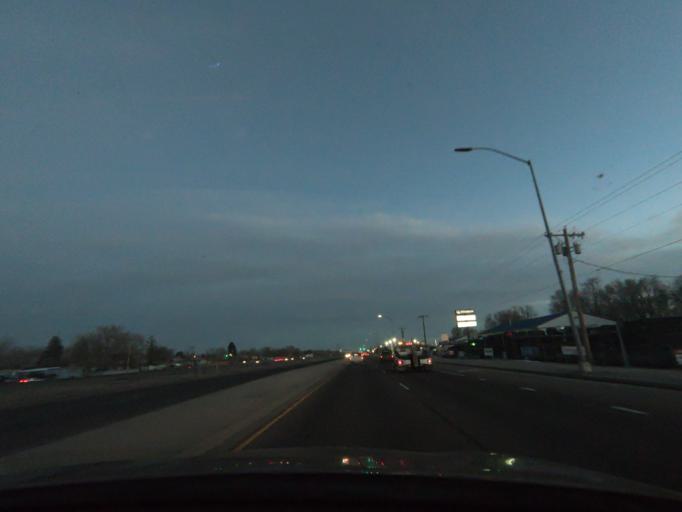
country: US
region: Colorado
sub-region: El Paso County
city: Security-Widefield
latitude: 38.7489
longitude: -104.7422
